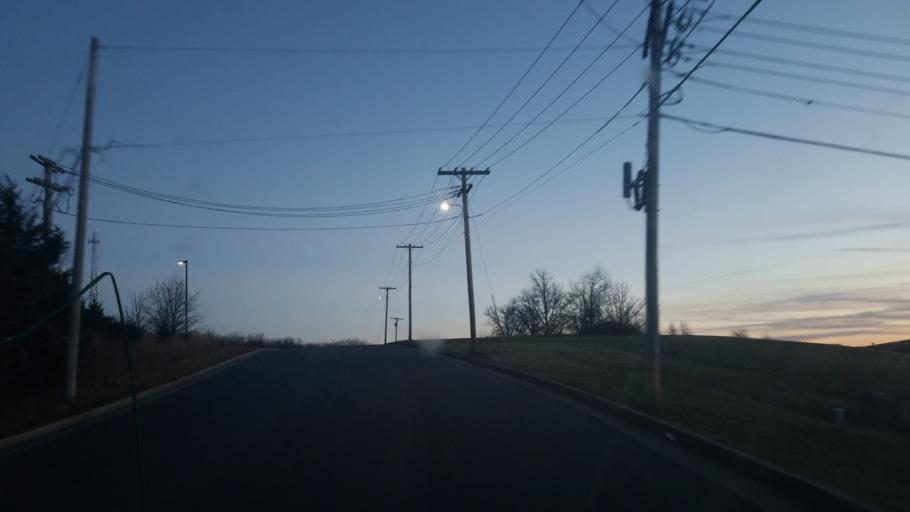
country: US
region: Missouri
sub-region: Howell County
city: West Plains
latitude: 36.7283
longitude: -91.8762
